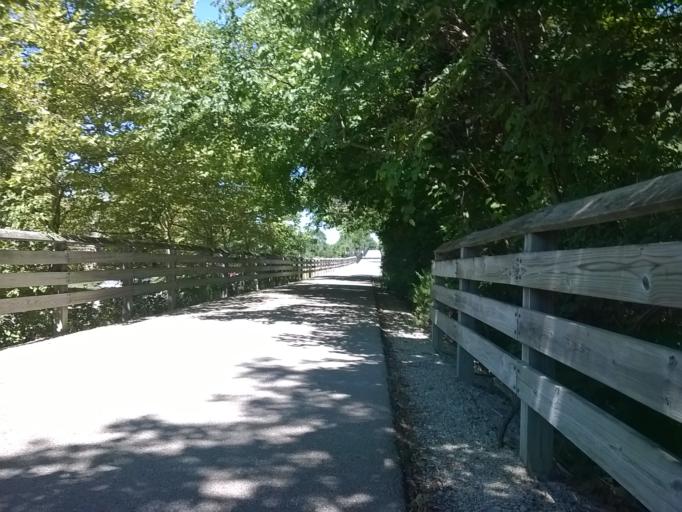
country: US
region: Indiana
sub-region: Hamilton County
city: Carmel
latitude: 39.9975
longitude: -86.1364
